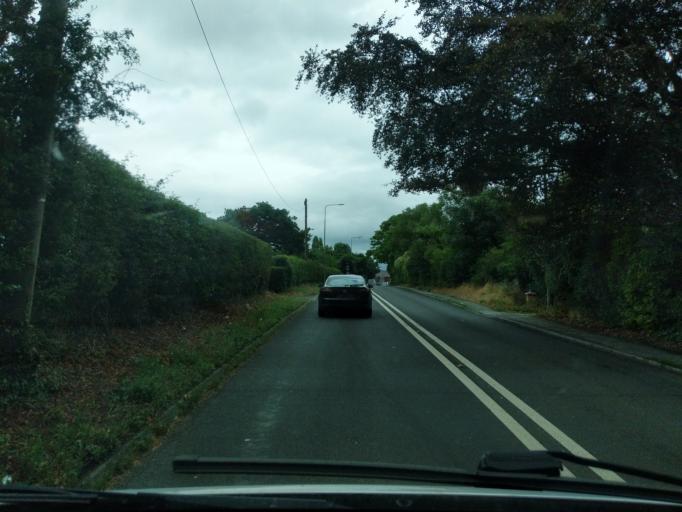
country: GB
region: England
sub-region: Cheshire West and Chester
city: Cuddington
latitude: 53.2382
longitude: -2.6024
